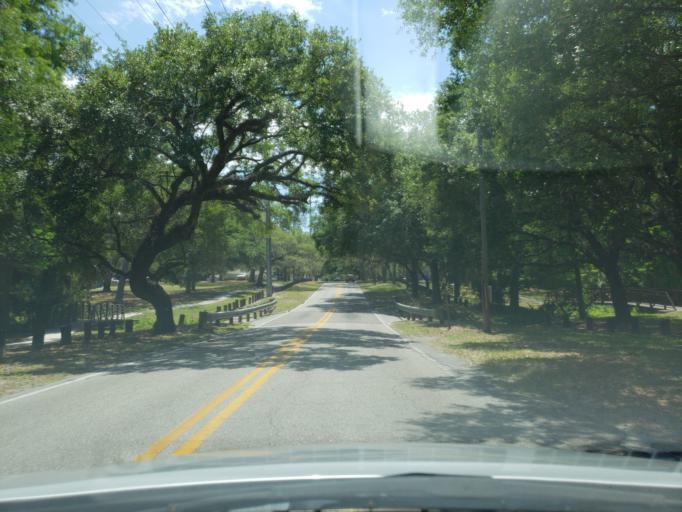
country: US
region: Florida
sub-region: Hillsborough County
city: Egypt Lake-Leto
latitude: 28.0135
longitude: -82.4678
